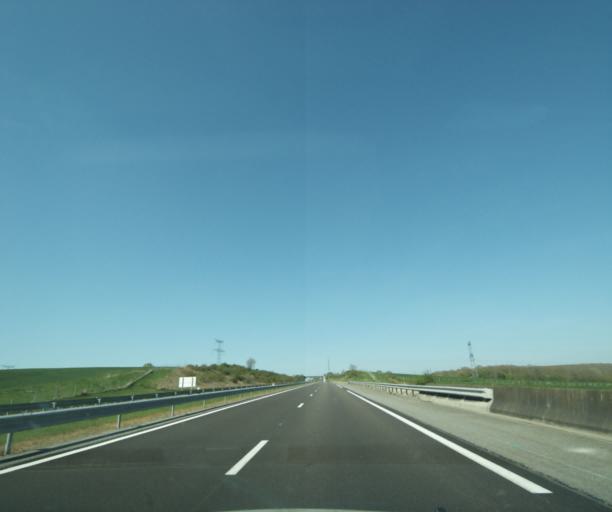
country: FR
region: Bourgogne
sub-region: Departement de la Nievre
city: Cosne-Cours-sur-Loire
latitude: 47.4531
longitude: 2.9481
